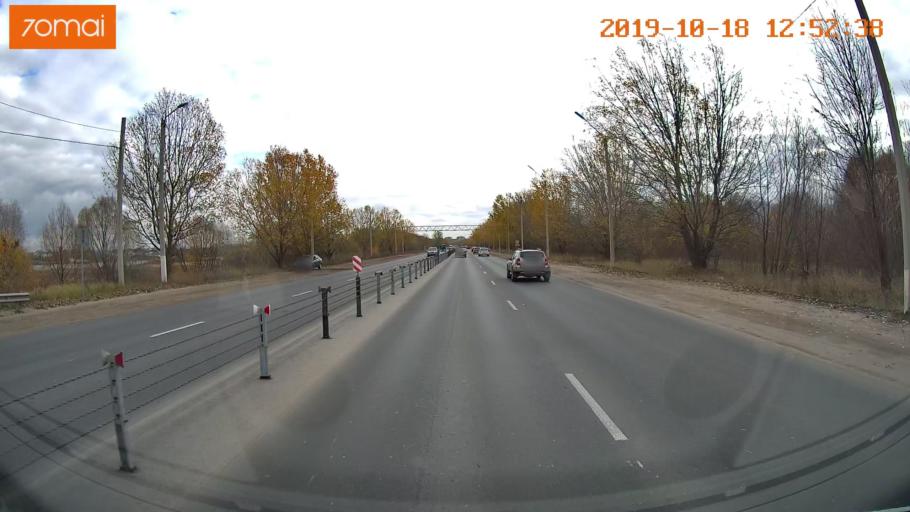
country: RU
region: Rjazan
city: Ryazan'
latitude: 54.6507
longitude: 39.6962
